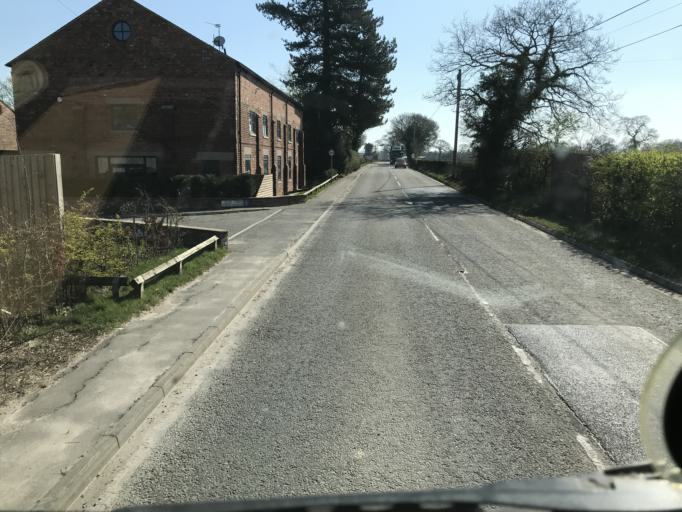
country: GB
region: England
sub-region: Cheshire East
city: Mobberley
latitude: 53.2772
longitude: -2.3007
